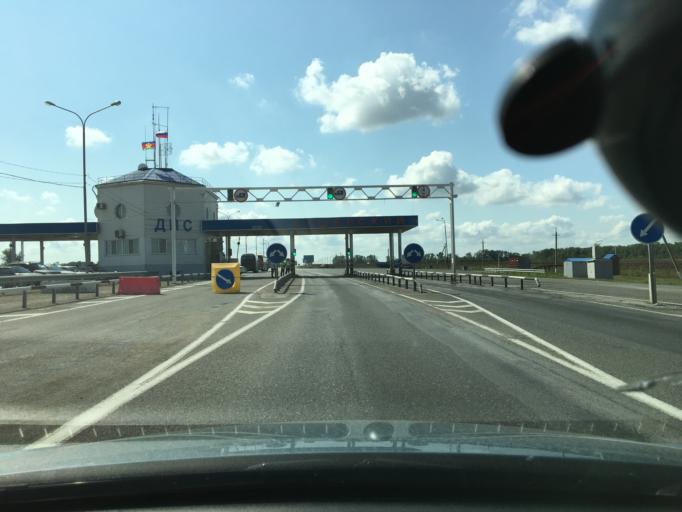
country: RU
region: Krasnodarskiy
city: Krasnoye
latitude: 46.7600
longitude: 39.6611
